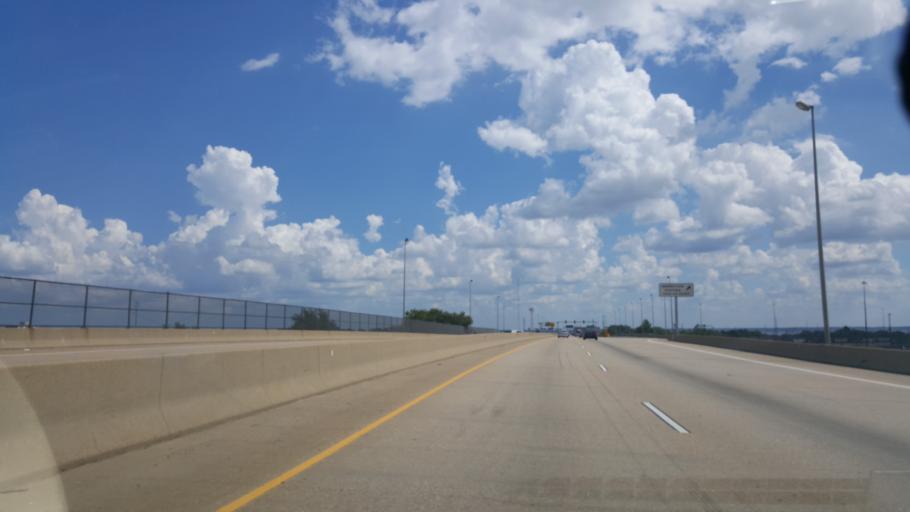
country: US
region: Virginia
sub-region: City of Newport News
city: Newport News
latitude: 36.9741
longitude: -76.4202
